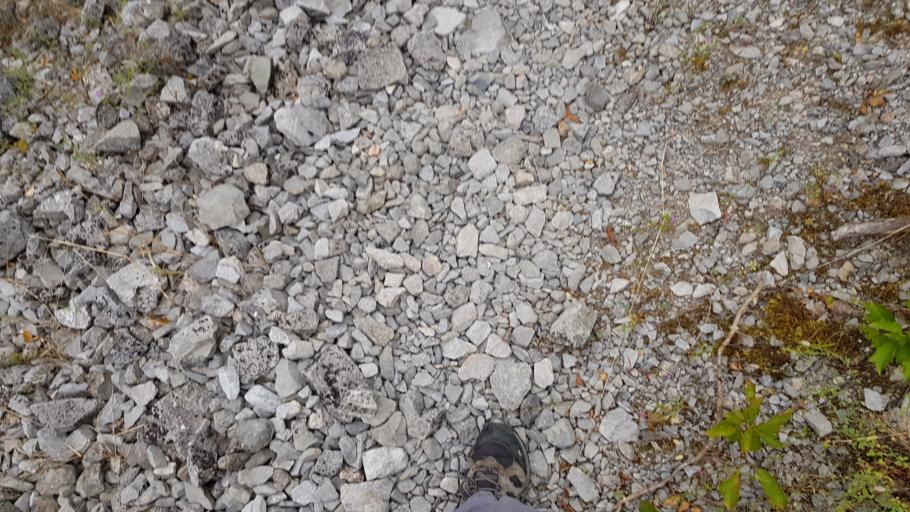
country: ES
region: La Rioja
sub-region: Provincia de La Rioja
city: Nestares
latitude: 42.2592
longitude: -2.6118
